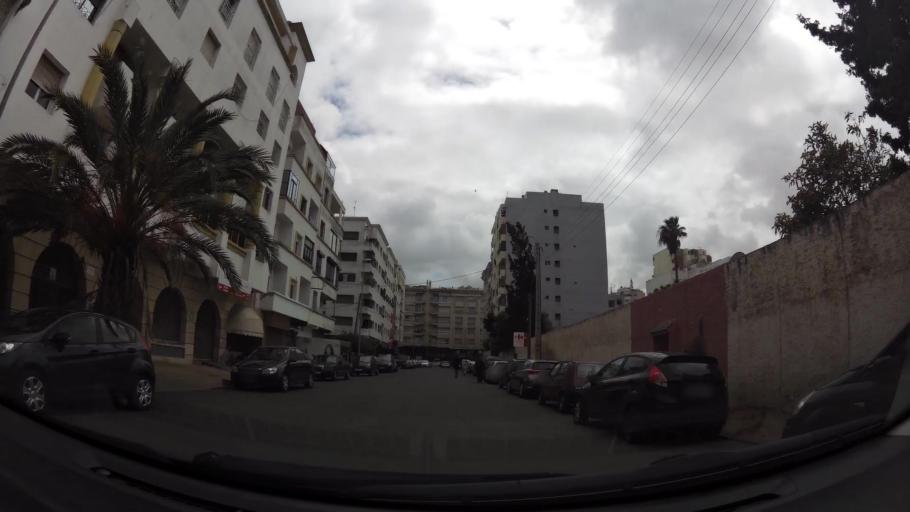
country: MA
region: Grand Casablanca
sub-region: Casablanca
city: Casablanca
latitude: 33.5956
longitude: -7.6423
